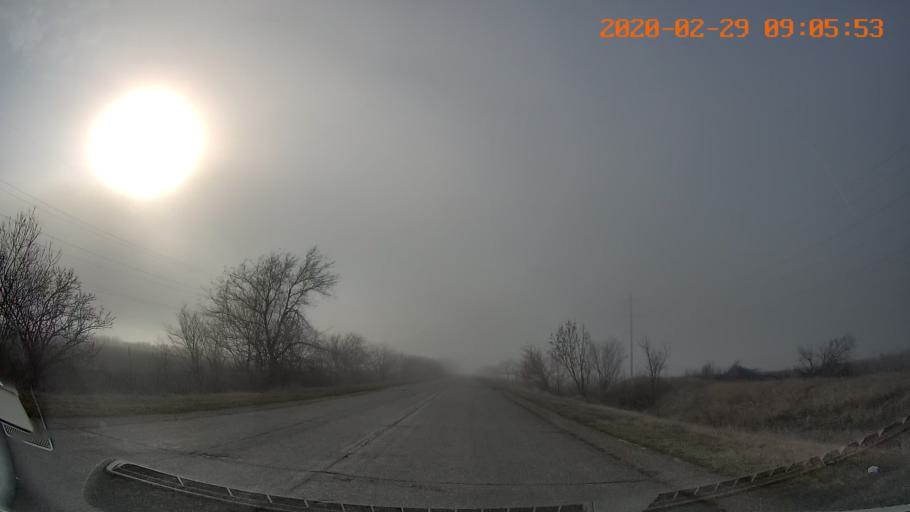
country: MD
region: Telenesti
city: Tiraspolul Nou
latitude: 46.8832
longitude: 29.7425
